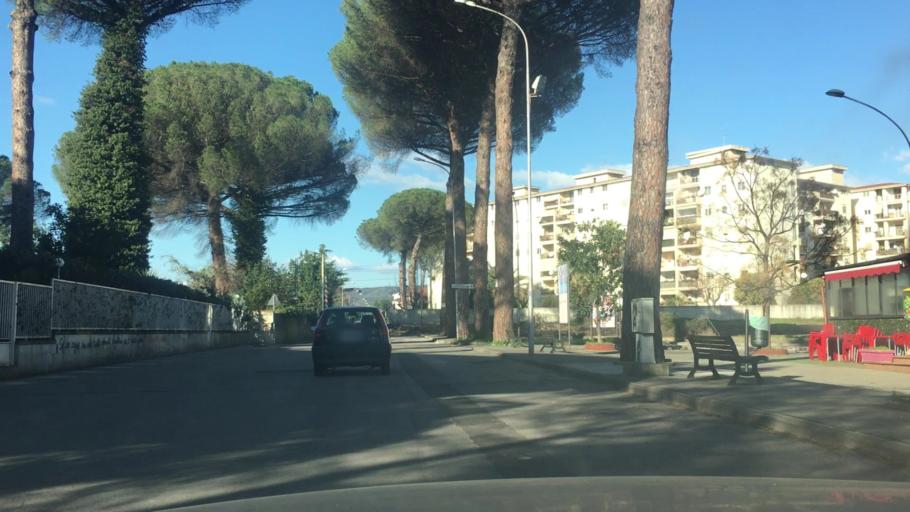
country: IT
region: Campania
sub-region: Provincia di Caserta
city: Caserta
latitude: 41.0673
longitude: 14.3538
